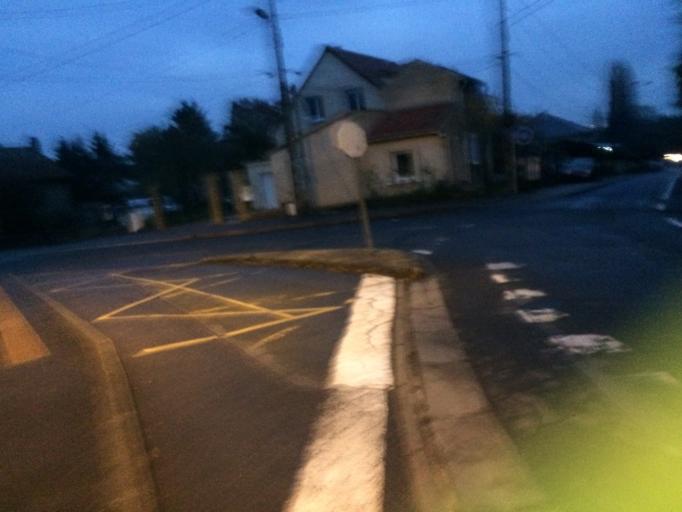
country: FR
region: Ile-de-France
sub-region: Departement de l'Essonne
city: Nozay
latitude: 48.6638
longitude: 2.2500
